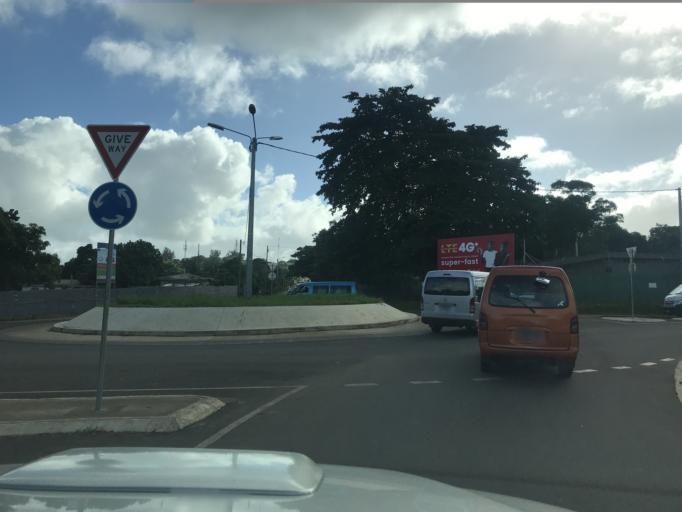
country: VU
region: Shefa
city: Port-Vila
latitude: -17.7433
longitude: 168.3173
